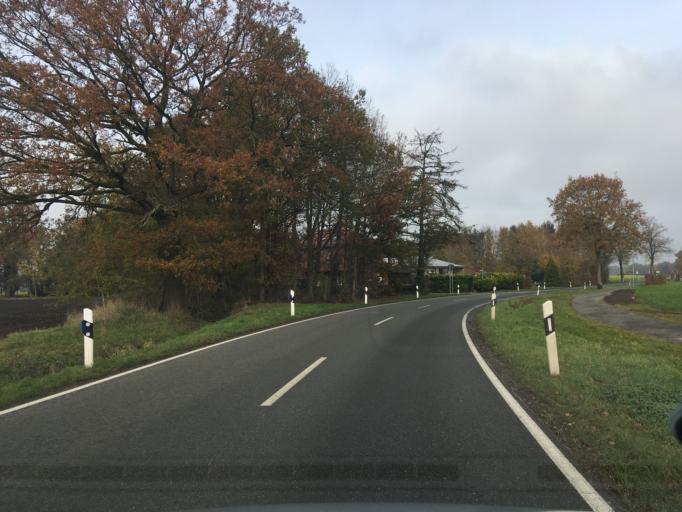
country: DE
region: North Rhine-Westphalia
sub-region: Regierungsbezirk Munster
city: Sudlohn
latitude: 51.9091
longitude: 6.9164
